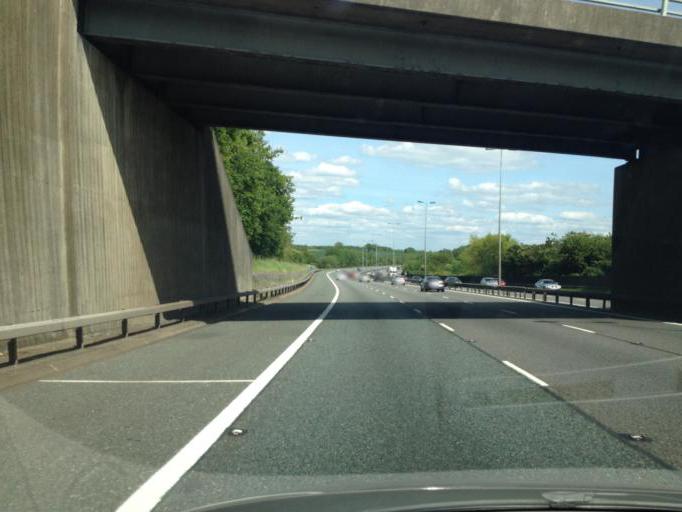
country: GB
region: England
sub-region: Buckinghamshire
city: Stokenchurch
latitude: 51.6252
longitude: -0.8363
